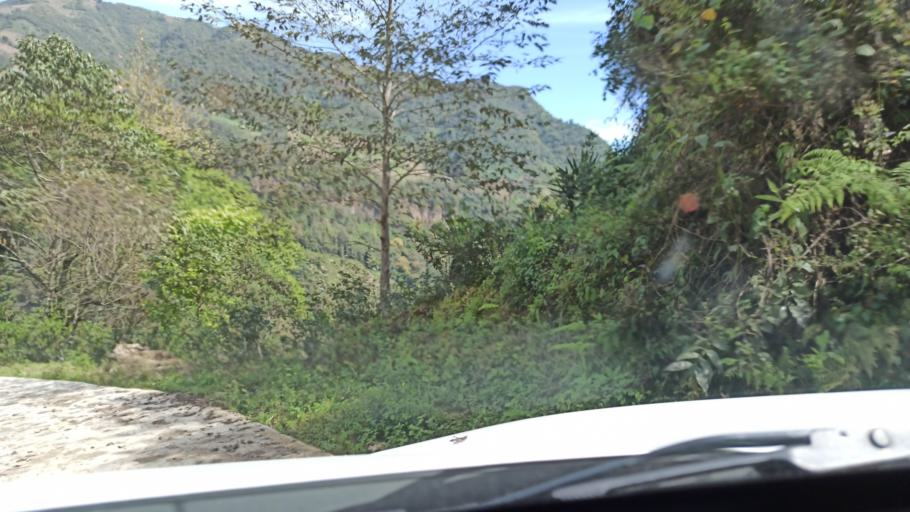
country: MX
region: Veracruz
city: Xocotla
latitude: 18.9827
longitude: -97.0977
